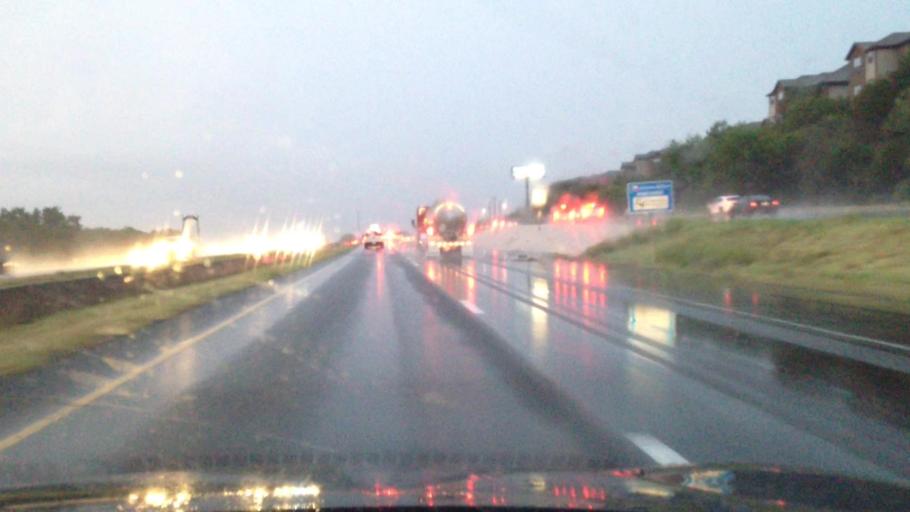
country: US
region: Texas
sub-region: Bexar County
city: Shavano Park
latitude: 29.6019
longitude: -98.5569
